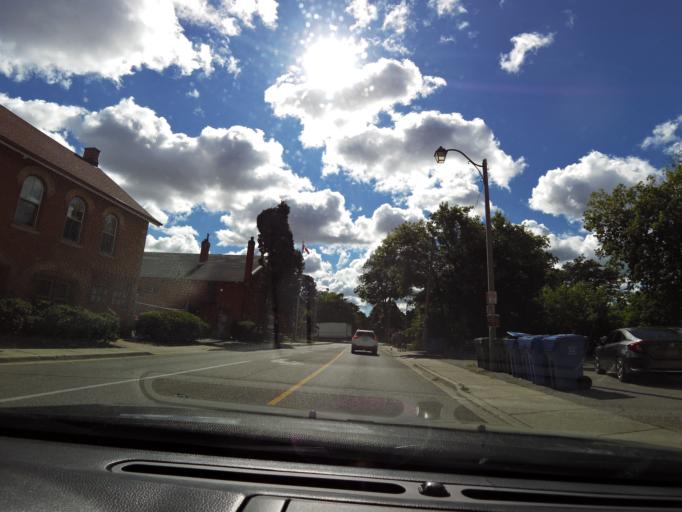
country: CA
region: Ontario
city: Brampton
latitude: 43.6869
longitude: -79.7586
